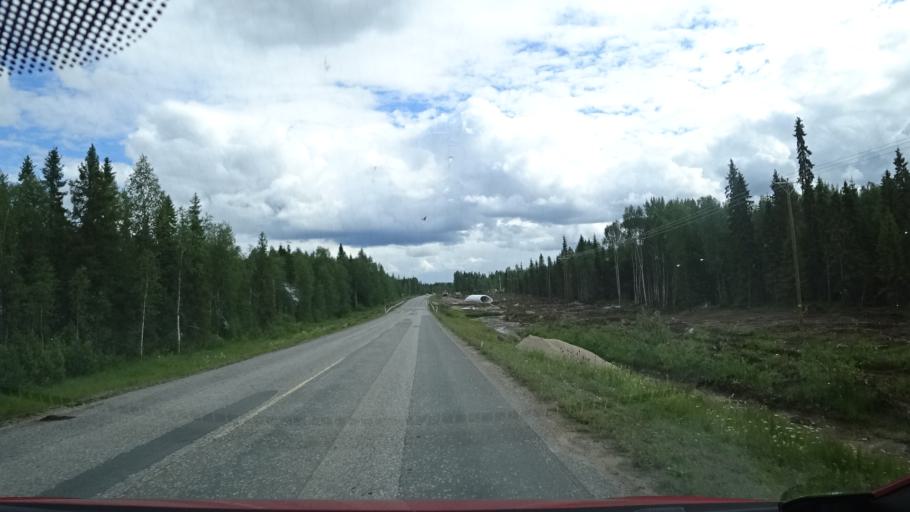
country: FI
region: Lapland
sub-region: Rovaniemi
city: Rovaniemi
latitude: 66.5396
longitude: 25.7196
